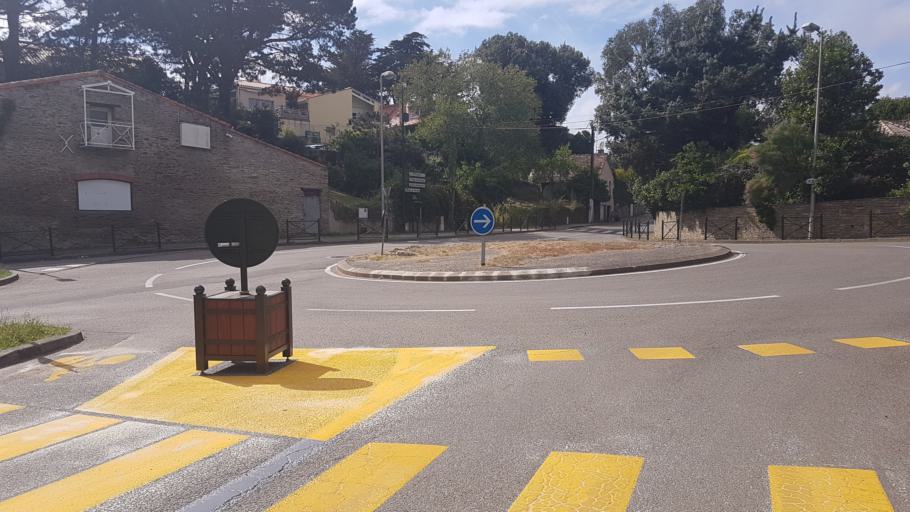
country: FR
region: Pays de la Loire
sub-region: Departement de la Loire-Atlantique
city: La Plaine-sur-Mer
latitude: 47.1147
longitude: -2.1467
